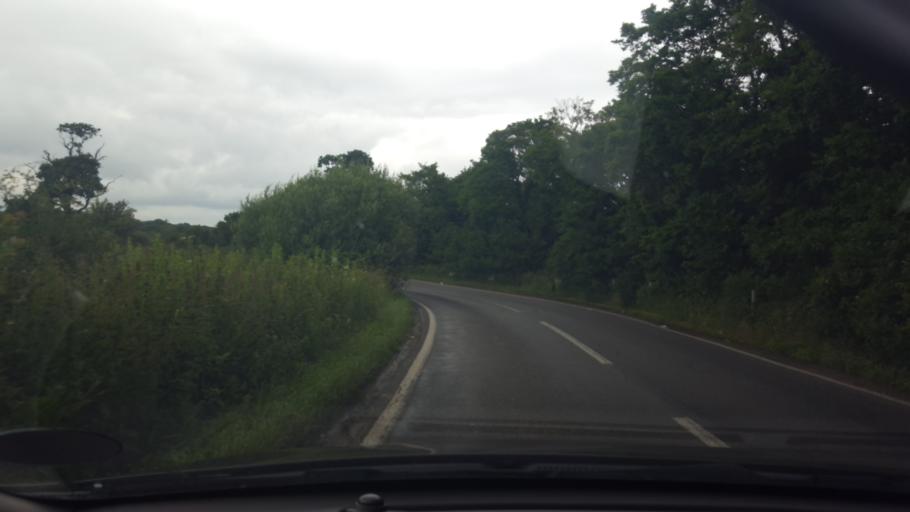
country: GB
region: England
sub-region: Essex
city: Little Clacton
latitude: 51.8123
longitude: 1.1270
